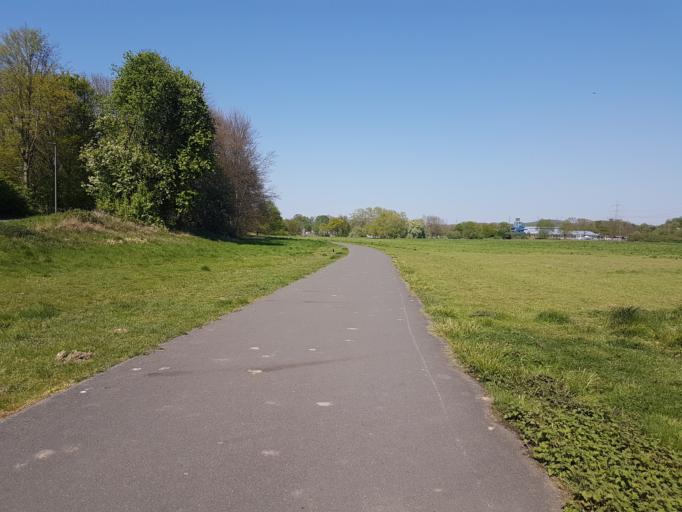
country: DE
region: North Rhine-Westphalia
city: Witten
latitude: 51.4332
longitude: 7.2779
